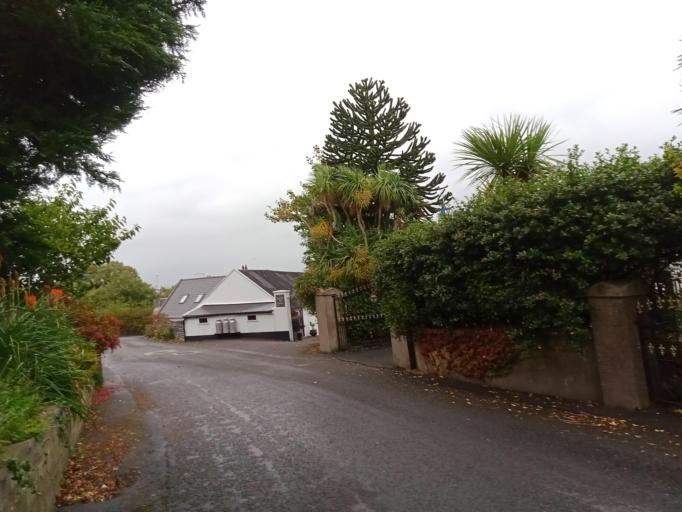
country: IE
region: Munster
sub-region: Waterford
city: Dungarvan
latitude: 52.0473
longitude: -7.5663
